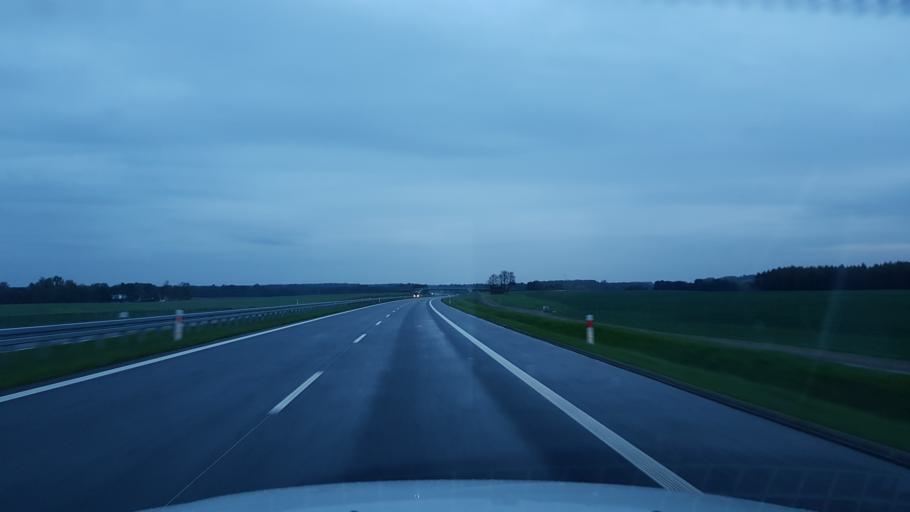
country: PL
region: West Pomeranian Voivodeship
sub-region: Powiat gryficki
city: Brojce
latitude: 53.9197
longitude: 15.3839
